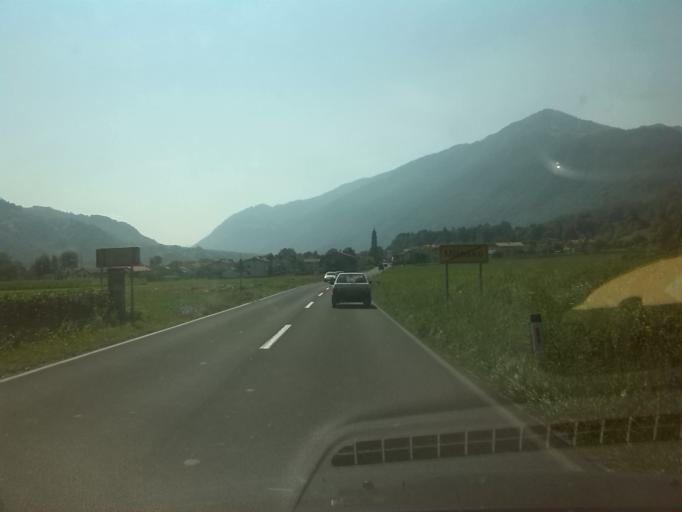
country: SI
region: Kobarid
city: Kobarid
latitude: 46.2361
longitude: 13.5867
